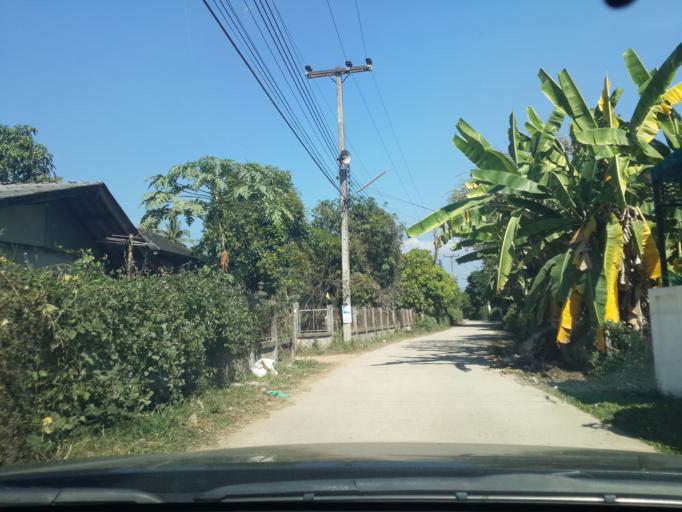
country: TH
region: Chiang Mai
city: San Sai
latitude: 18.8812
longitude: 99.1104
